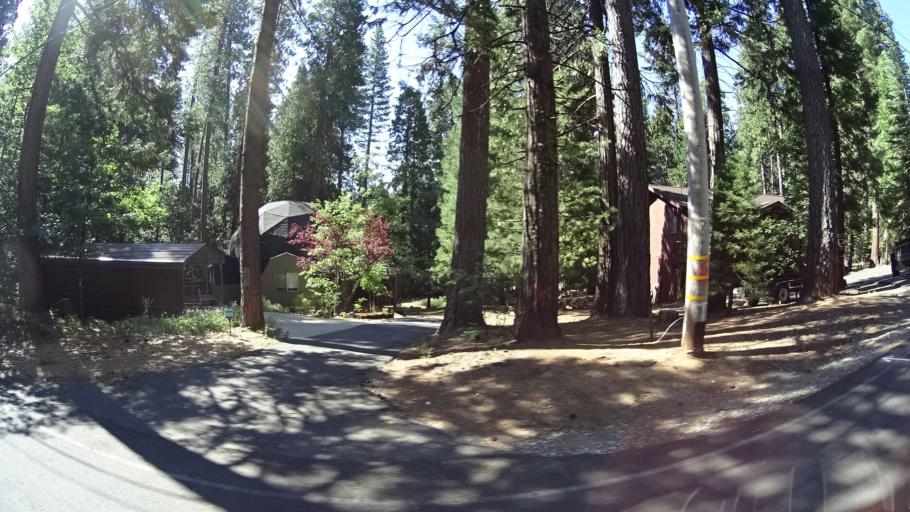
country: US
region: California
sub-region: Calaveras County
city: Arnold
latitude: 38.2382
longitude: -120.3704
